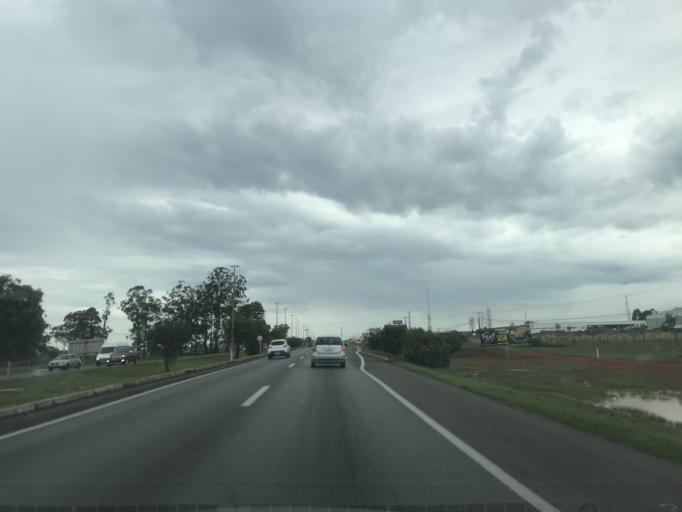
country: BR
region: Goias
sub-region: Luziania
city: Luziania
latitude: -16.0146
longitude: -47.9818
